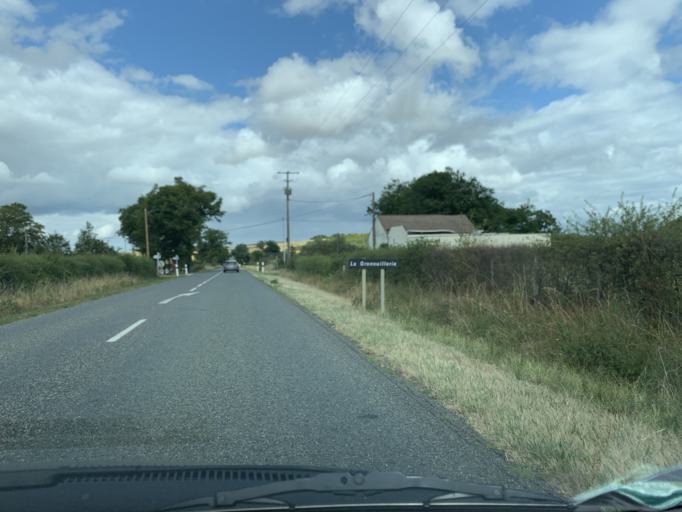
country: FR
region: Bourgogne
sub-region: Departement de la Nievre
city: Varzy
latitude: 47.3994
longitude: 3.4476
